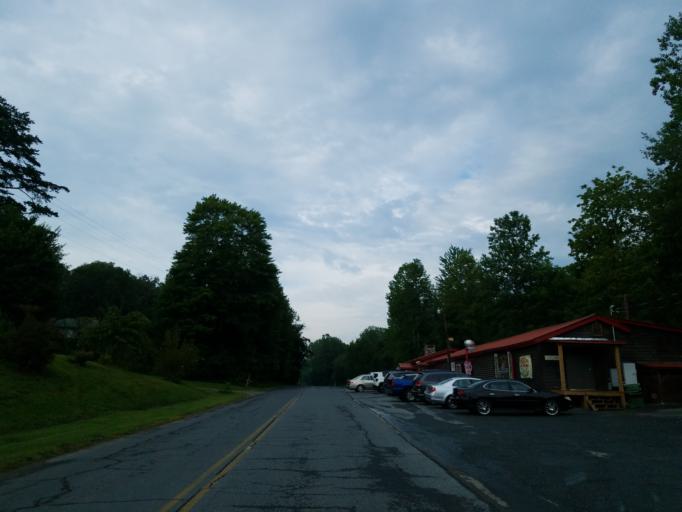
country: US
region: Georgia
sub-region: Fannin County
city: Blue Ridge
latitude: 34.7881
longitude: -84.3848
